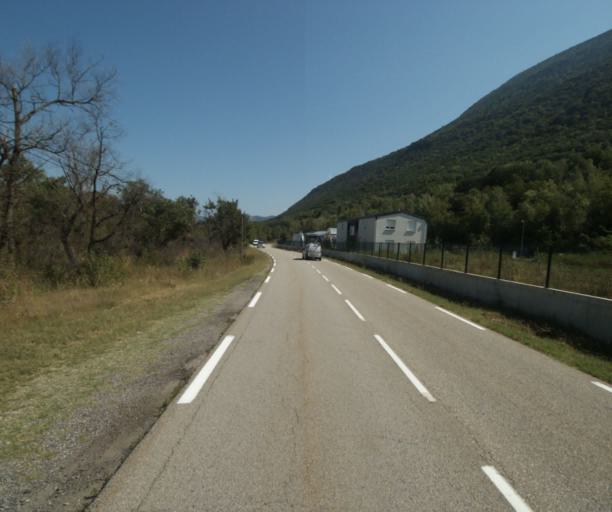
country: FR
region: Rhone-Alpes
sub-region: Departement de l'Isere
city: Saint-Georges-de-Commiers
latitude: 45.0507
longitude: 5.7084
